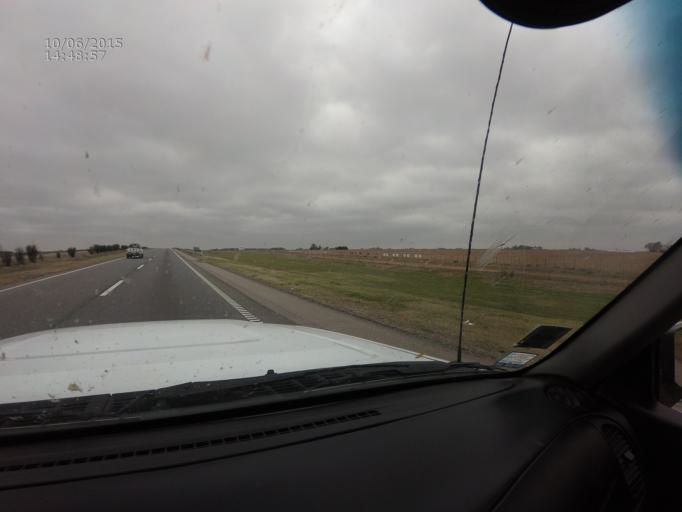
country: AR
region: Cordoba
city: Oncativo
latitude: -31.9357
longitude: -63.6115
